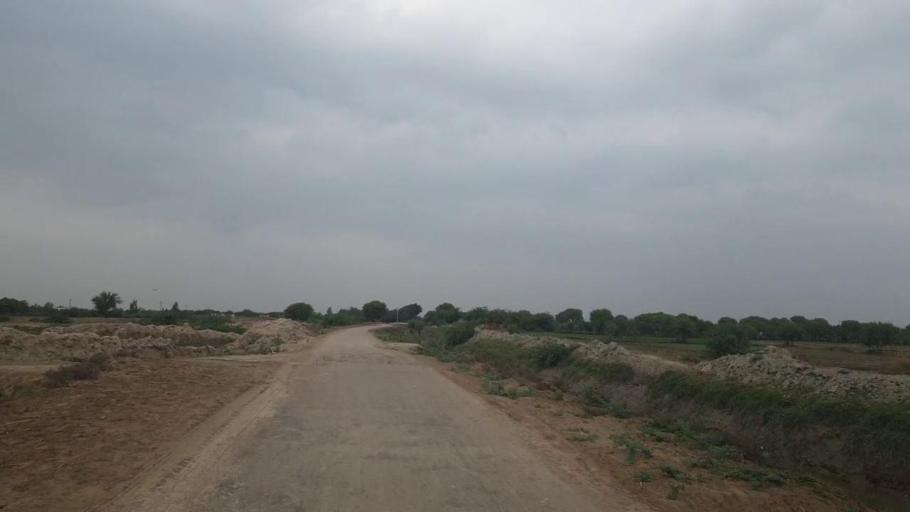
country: PK
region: Sindh
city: Badin
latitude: 24.6291
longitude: 68.6817
